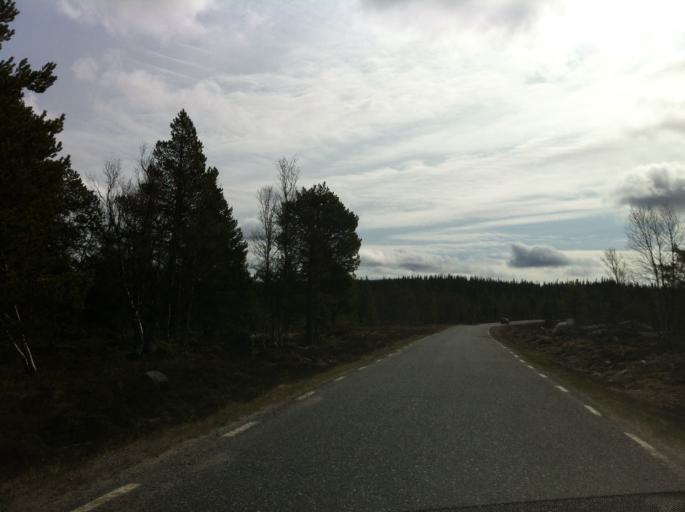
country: NO
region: Hedmark
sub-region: Engerdal
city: Engerdal
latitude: 62.3185
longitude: 12.8087
